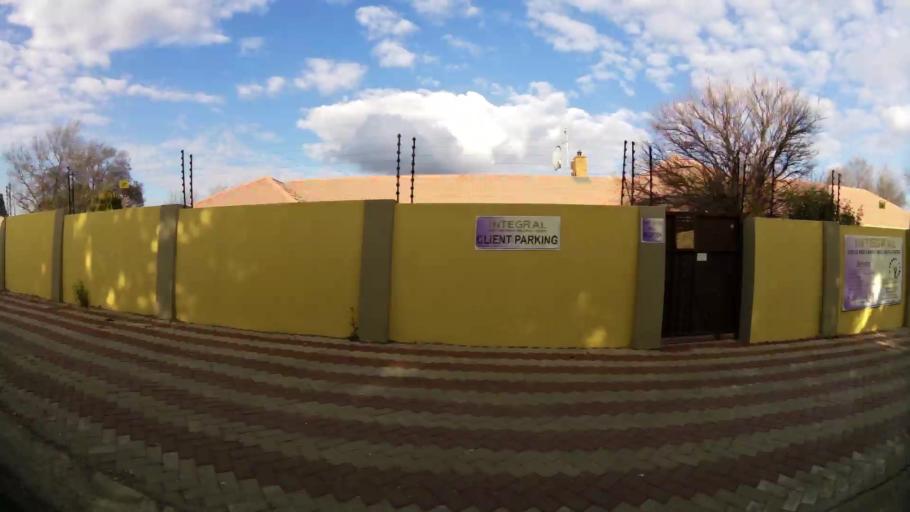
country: ZA
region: Orange Free State
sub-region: Mangaung Metropolitan Municipality
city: Bloemfontein
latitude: -29.1019
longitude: 26.1976
